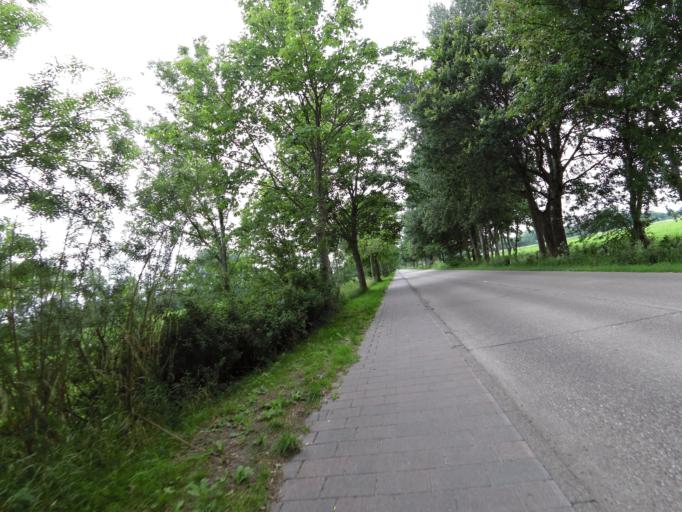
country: DE
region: Lower Saxony
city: Padingbuttel
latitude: 53.7249
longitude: 8.5370
